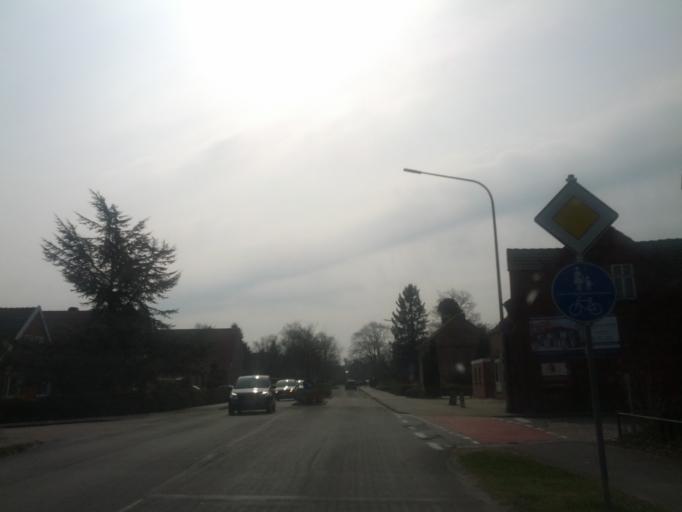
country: DE
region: Lower Saxony
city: Marienhafe
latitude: 53.5264
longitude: 7.2716
